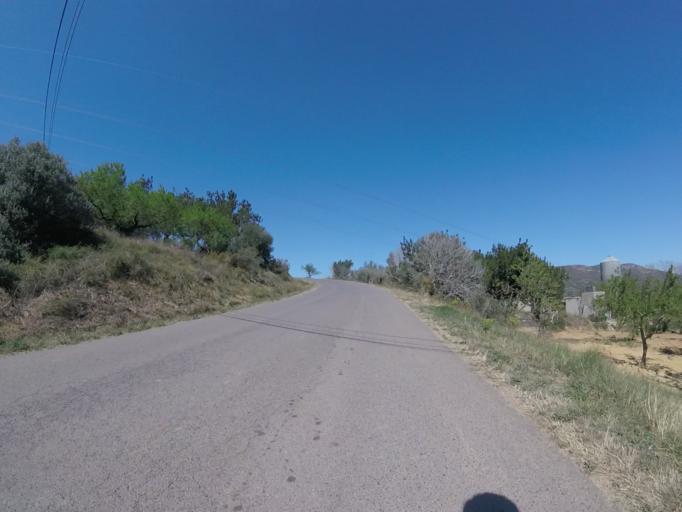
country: ES
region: Valencia
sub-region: Provincia de Castello
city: Cuevas de Vinroma
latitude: 40.3795
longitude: 0.1397
